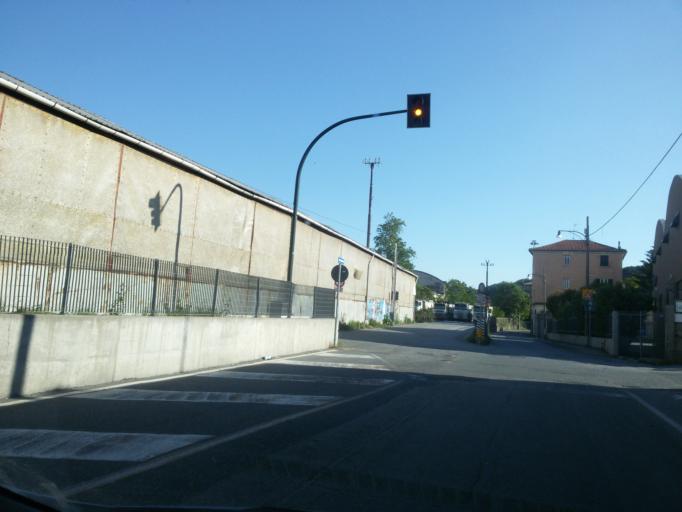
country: IT
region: Liguria
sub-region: Provincia di Genova
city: Genoa
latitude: 44.4510
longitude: 8.8905
